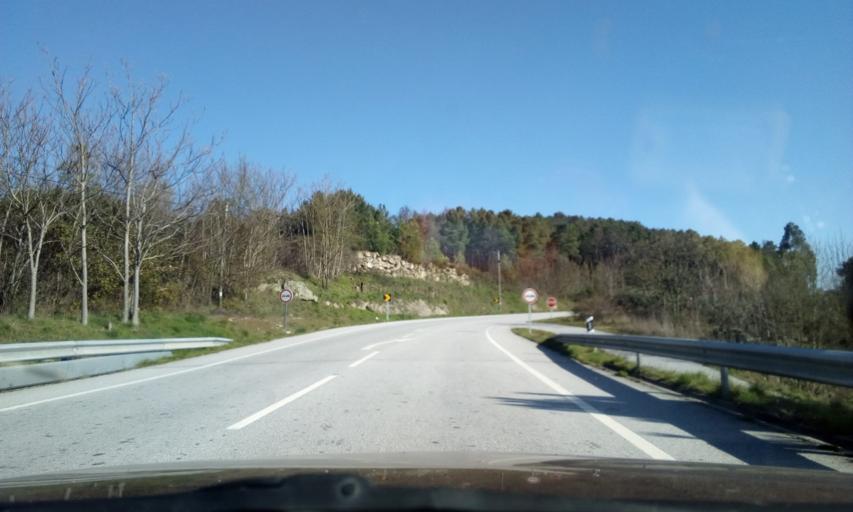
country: PT
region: Guarda
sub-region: Fornos de Algodres
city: Fornos de Algodres
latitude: 40.6204
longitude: -7.5113
